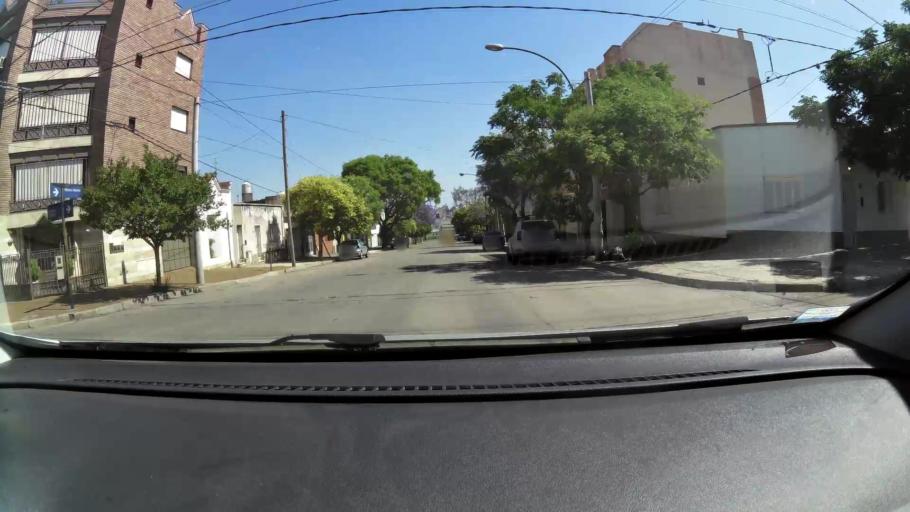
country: AR
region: Cordoba
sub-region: Departamento de Capital
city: Cordoba
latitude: -31.4027
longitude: -64.1797
